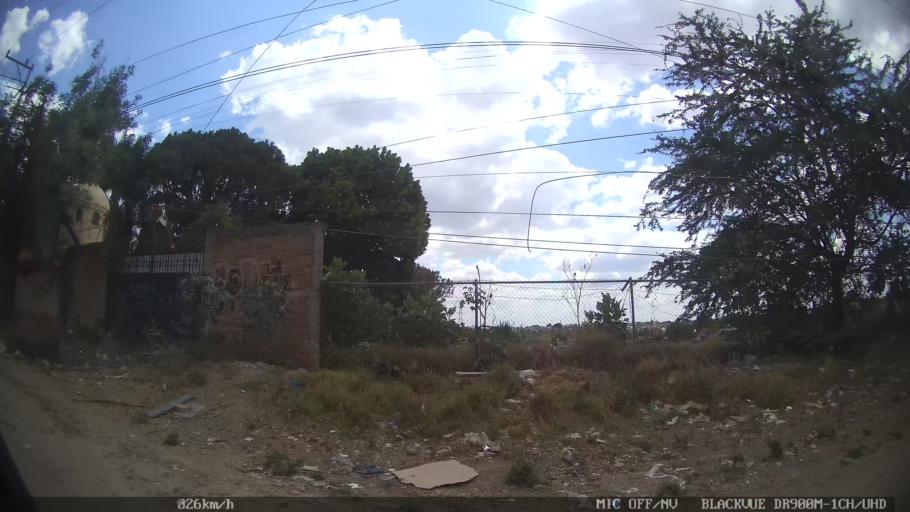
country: MX
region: Jalisco
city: Tlaquepaque
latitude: 20.6739
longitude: -103.2618
